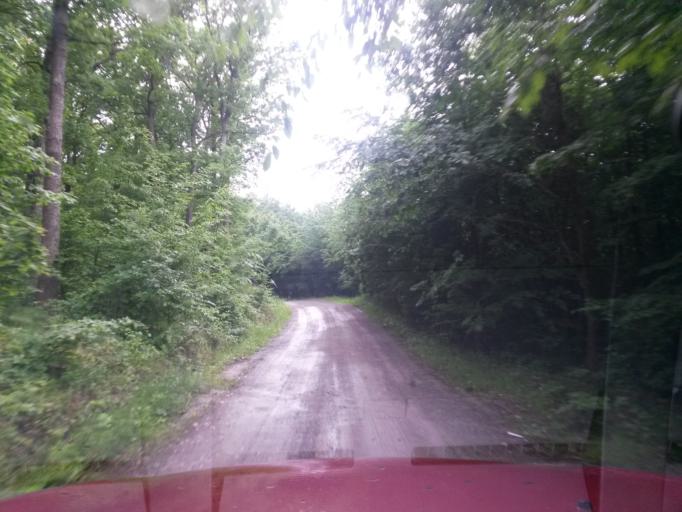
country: SK
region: Kosicky
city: Kosice
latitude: 48.7026
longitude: 21.1834
